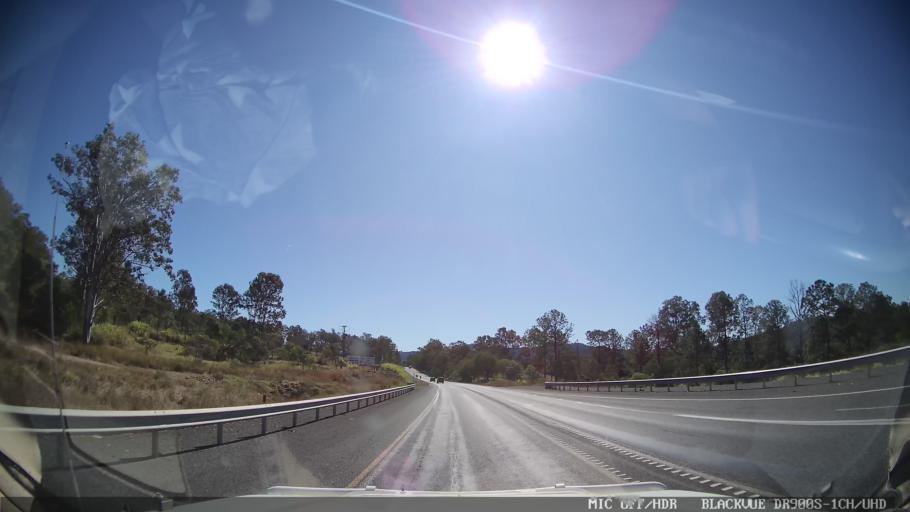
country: AU
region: Queensland
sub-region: Gympie Regional Council
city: Gympie
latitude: -26.0050
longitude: 152.5664
